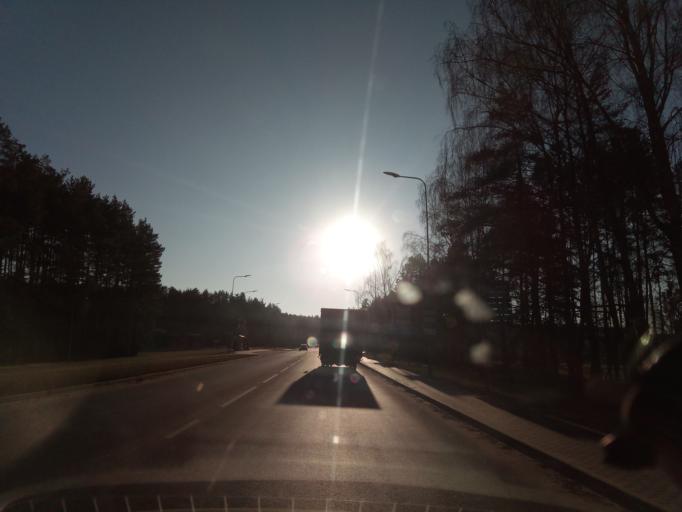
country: LT
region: Alytaus apskritis
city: Druskininkai
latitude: 54.0123
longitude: 23.9938
